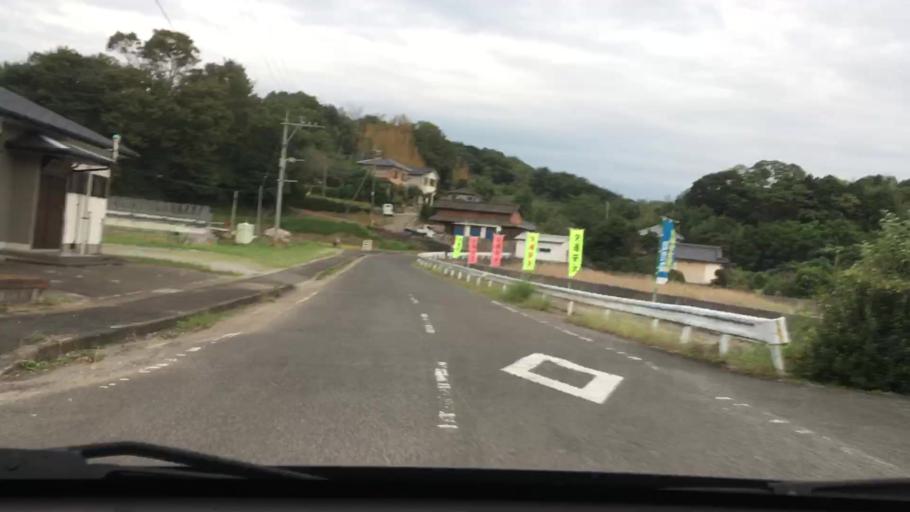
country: JP
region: Nagasaki
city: Sasebo
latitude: 33.0061
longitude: 129.7621
